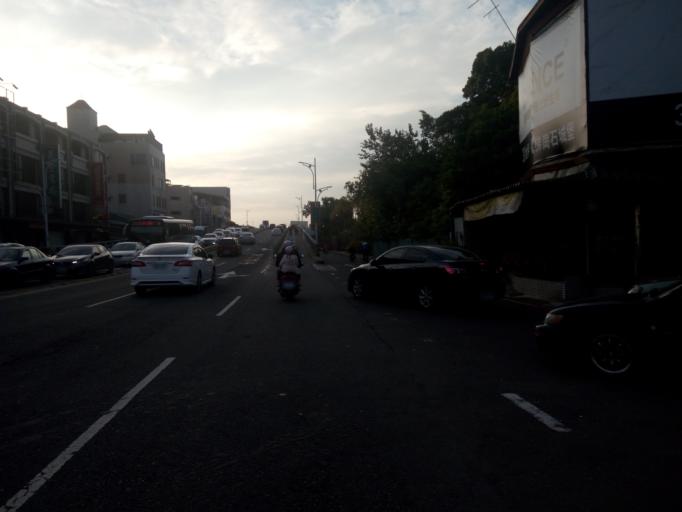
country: TW
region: Taiwan
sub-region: Chiayi
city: Jiayi Shi
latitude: 23.4751
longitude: 120.4391
